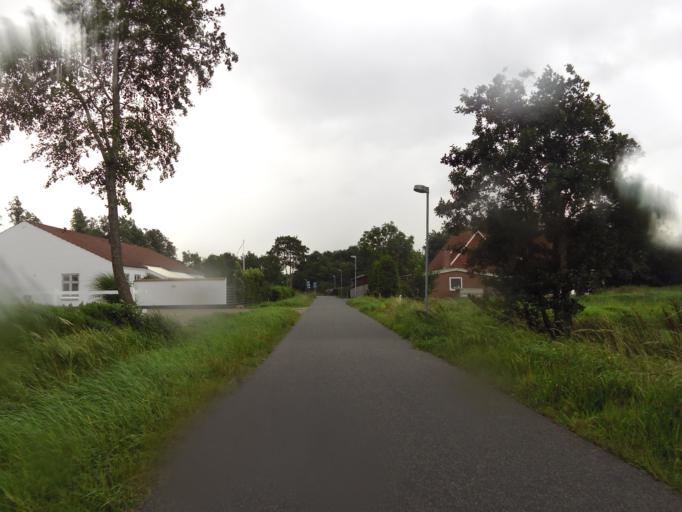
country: DK
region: South Denmark
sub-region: Esbjerg Kommune
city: Ribe
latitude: 55.3221
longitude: 8.7579
